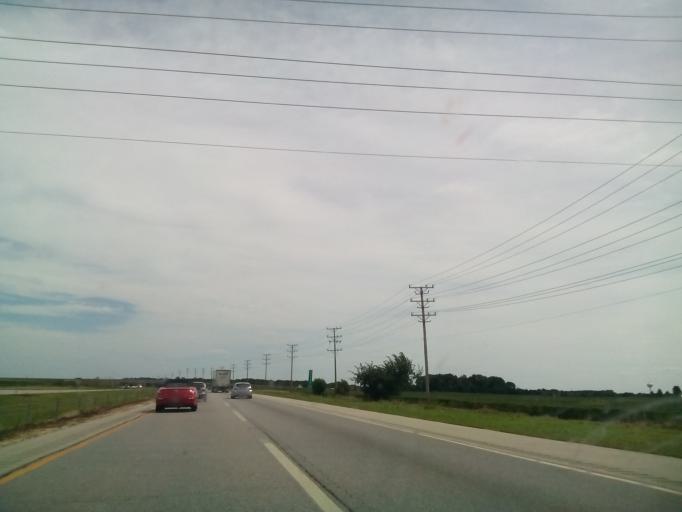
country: US
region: Illinois
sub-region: Kane County
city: Sugar Grove
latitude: 41.8052
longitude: -88.4351
